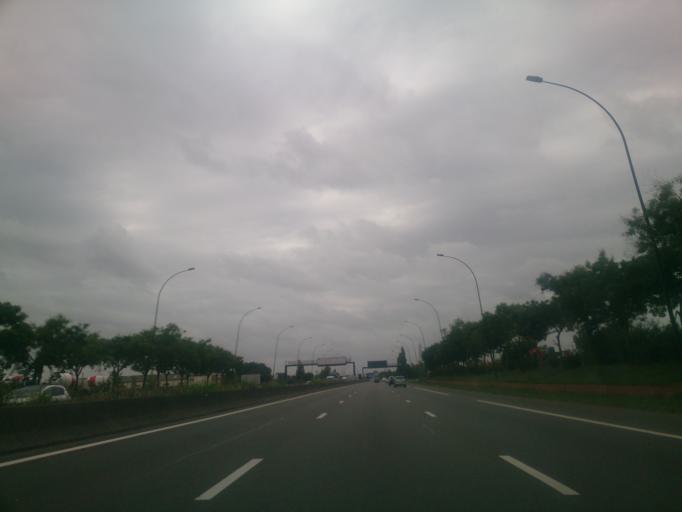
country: FR
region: Midi-Pyrenees
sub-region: Departement de la Haute-Garonne
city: Portet-sur-Garonne
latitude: 43.5451
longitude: 1.4010
